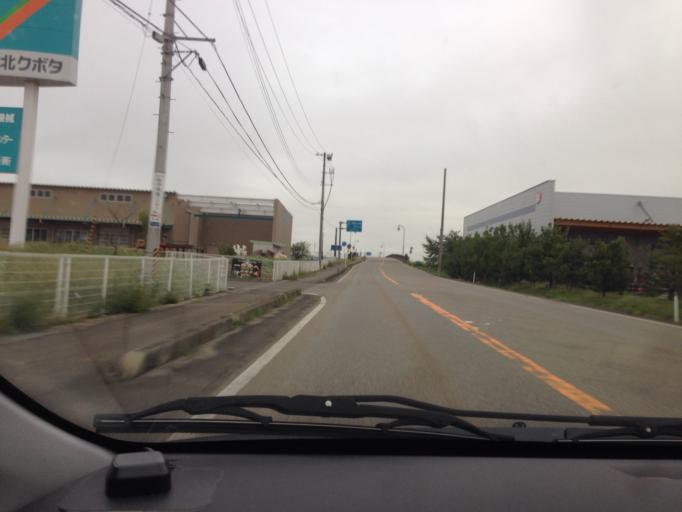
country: JP
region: Fukushima
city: Kitakata
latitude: 37.5879
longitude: 139.8929
